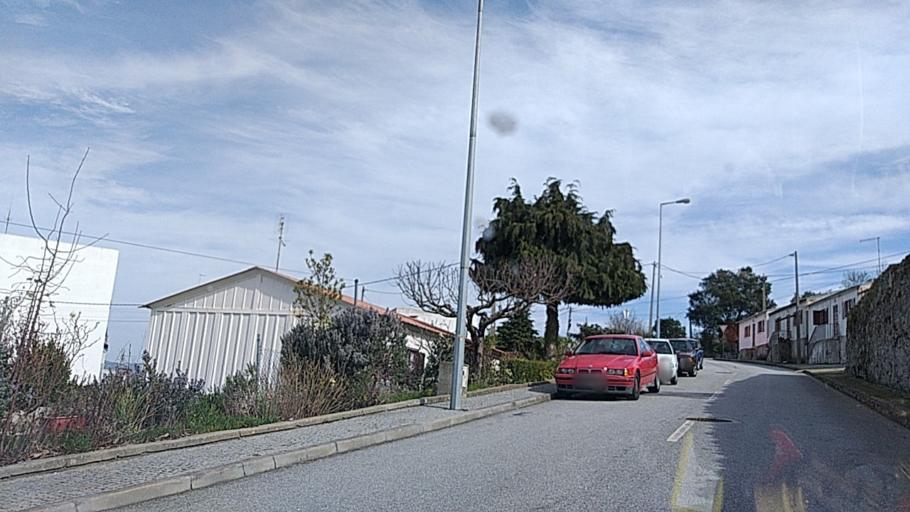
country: PT
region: Guarda
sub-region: Celorico da Beira
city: Celorico da Beira
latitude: 40.6401
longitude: -7.3917
